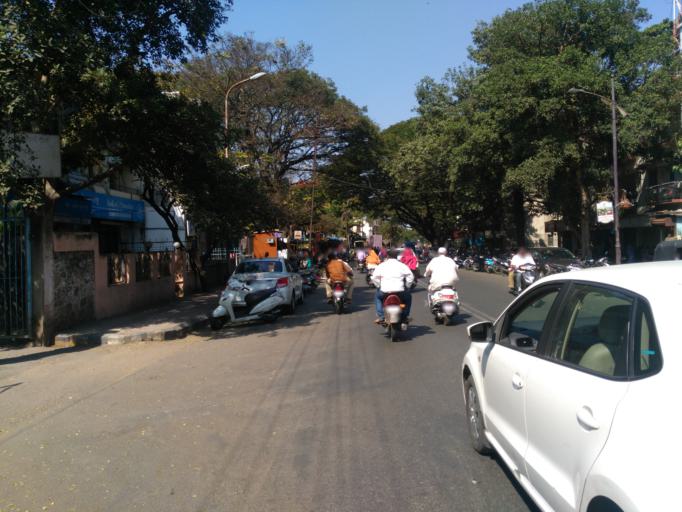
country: IN
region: Maharashtra
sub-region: Pune Division
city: Pune
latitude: 18.4886
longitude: 73.8498
